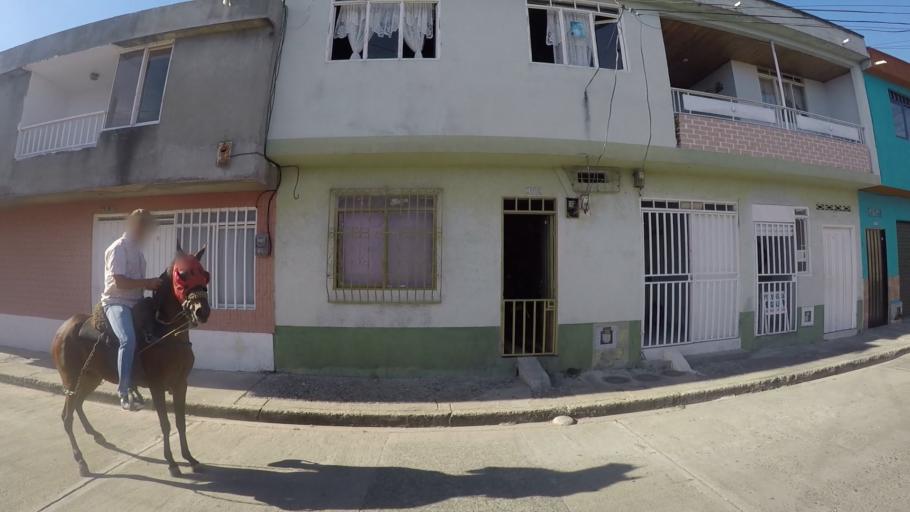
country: CO
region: Valle del Cauca
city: Cartago
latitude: 4.7535
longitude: -75.9216
